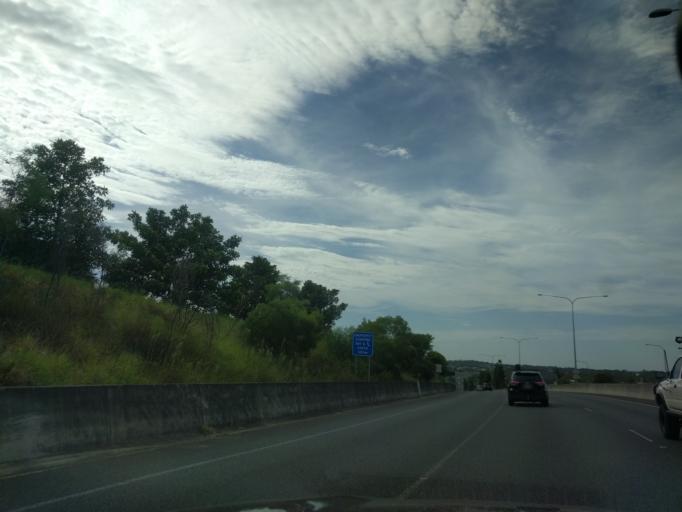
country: AU
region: Queensland
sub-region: Brisbane
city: Seventeen Mile Rocks
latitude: -27.5599
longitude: 152.9401
